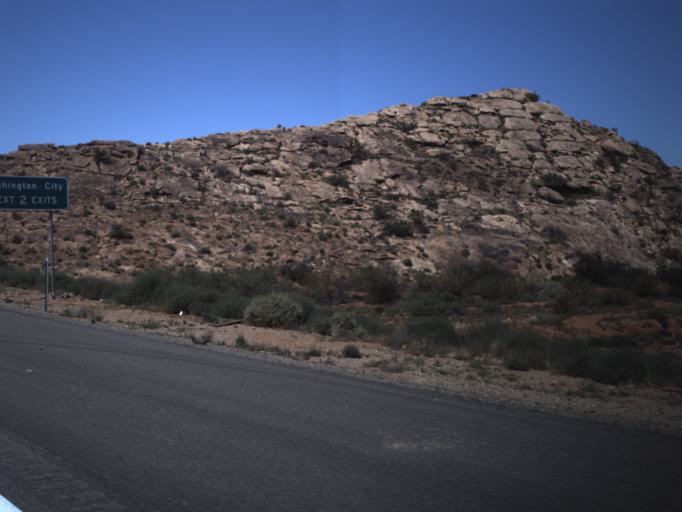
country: US
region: Utah
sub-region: Washington County
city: Washington
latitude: 37.1127
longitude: -113.4391
